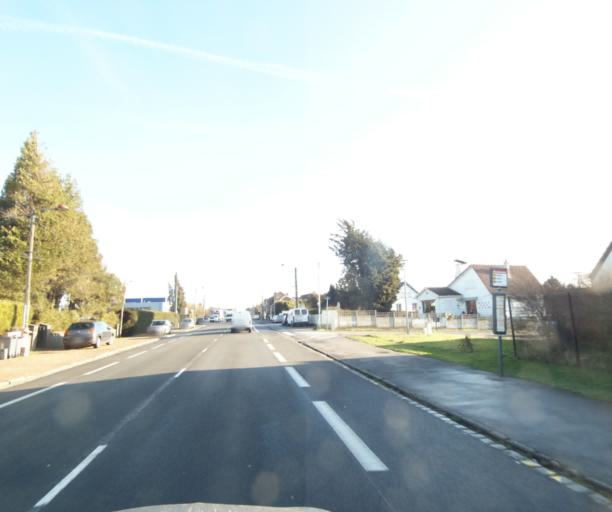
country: FR
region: Nord-Pas-de-Calais
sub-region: Departement du Nord
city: Marly
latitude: 50.3442
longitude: 3.5582
